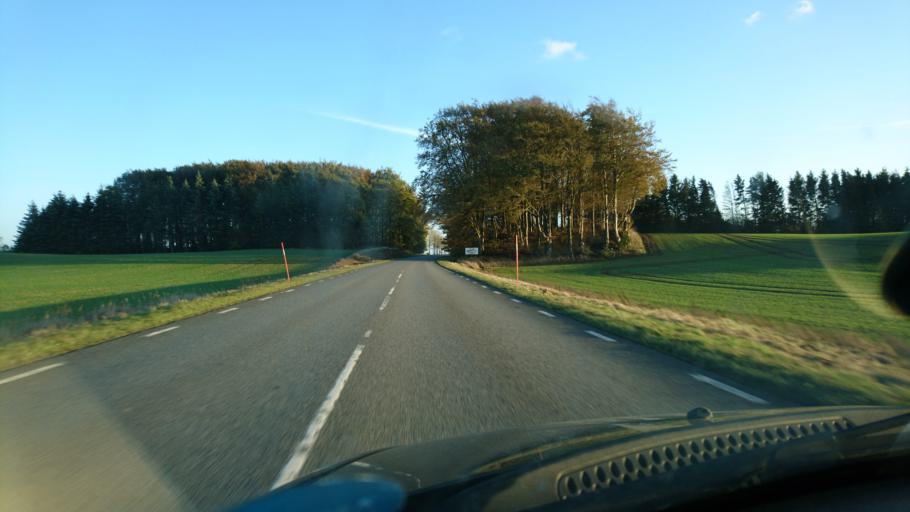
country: SE
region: Skane
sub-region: Simrishamns Kommun
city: Simrishamn
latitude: 55.4664
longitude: 14.1832
